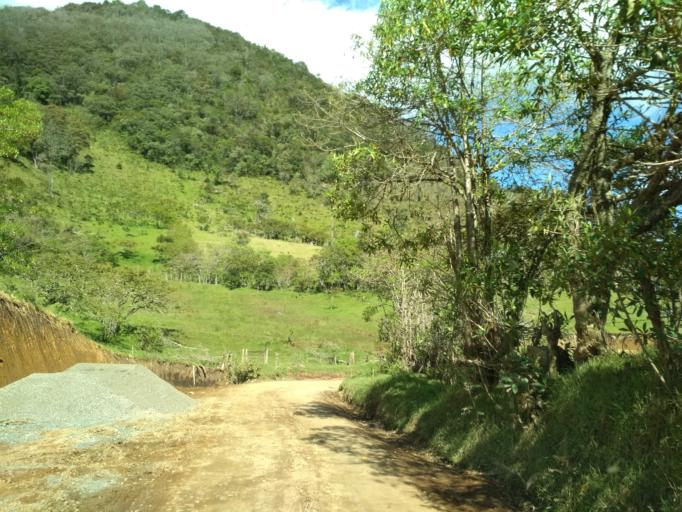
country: CO
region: Cauca
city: Jambalo
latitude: 2.7055
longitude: -76.3285
